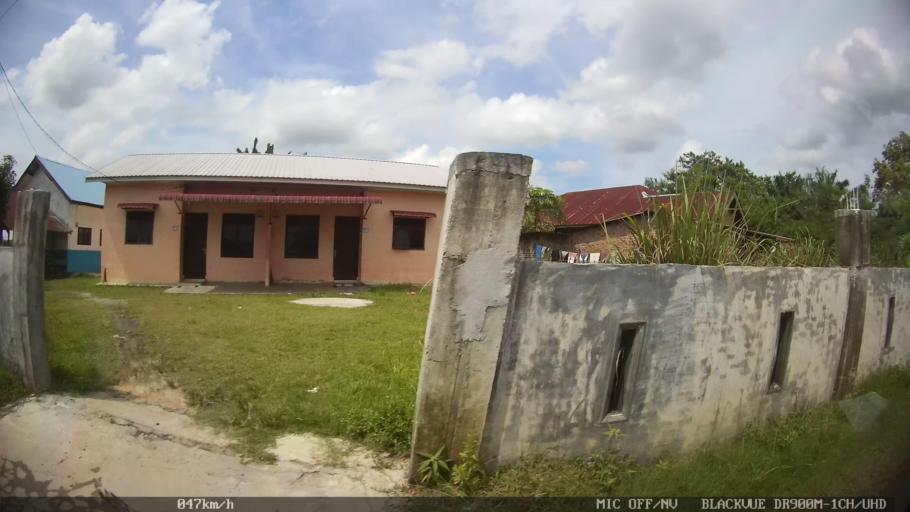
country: ID
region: North Sumatra
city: Percut
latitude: 3.5686
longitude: 98.8526
